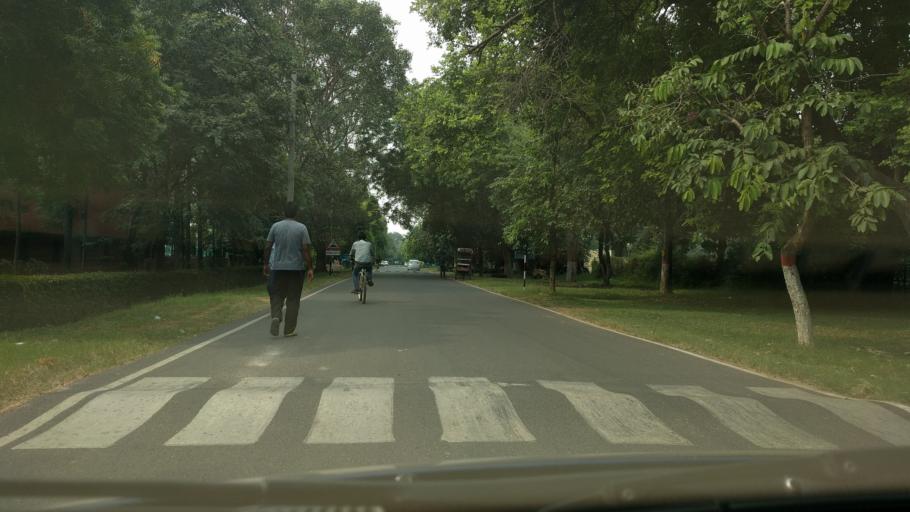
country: IN
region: NCT
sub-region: Central Delhi
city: Karol Bagh
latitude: 28.6341
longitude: 77.1618
